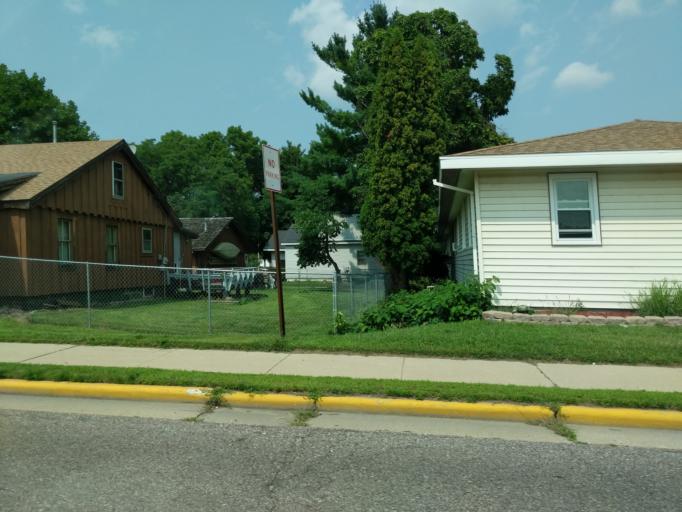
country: US
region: Wisconsin
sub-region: Columbia County
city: Portage
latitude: 43.5357
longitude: -89.4499
